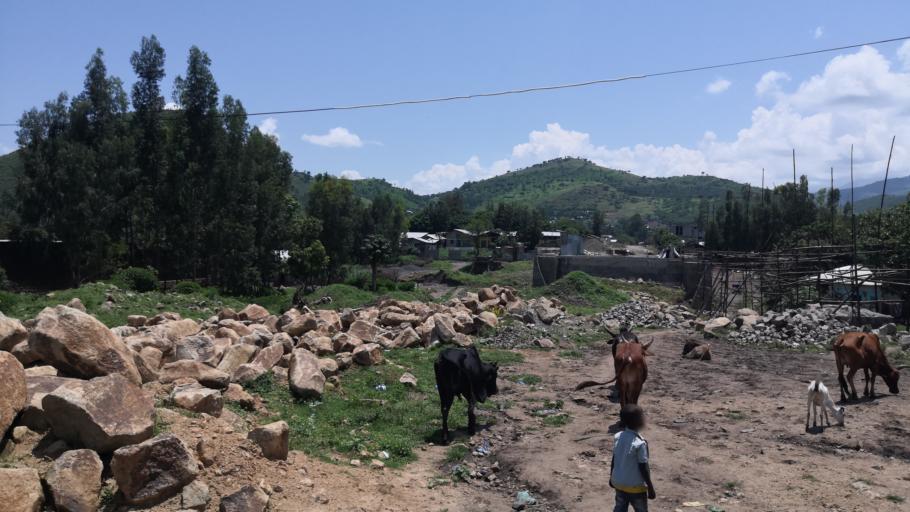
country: ET
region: Amhara
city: Abomsa
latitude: 10.3422
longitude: 39.9628
